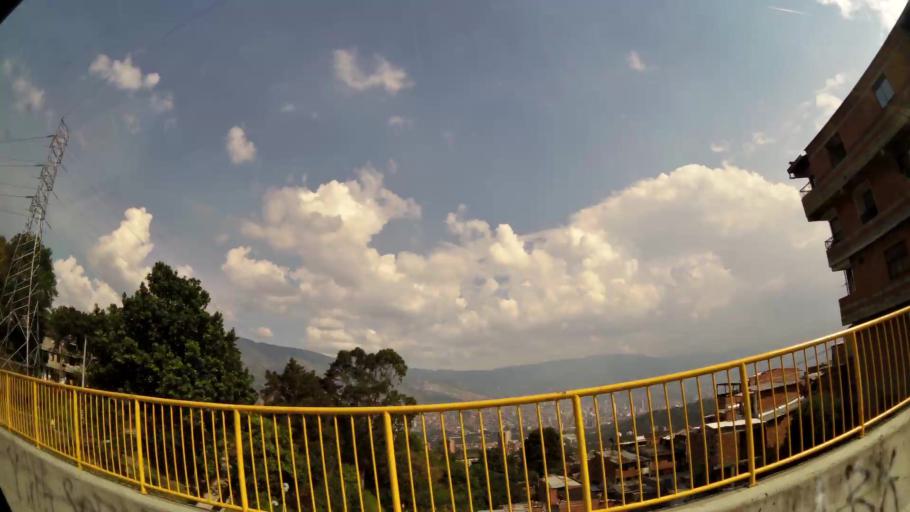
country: CO
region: Antioquia
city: Medellin
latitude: 6.2892
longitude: -75.5920
